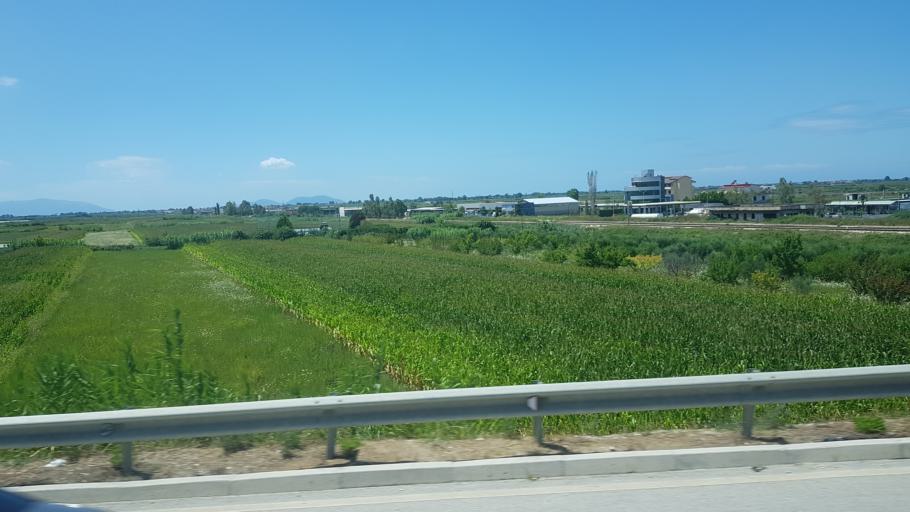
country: AL
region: Fier
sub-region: Rrethi i Fierit
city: Levan
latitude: 40.6682
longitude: 19.4860
